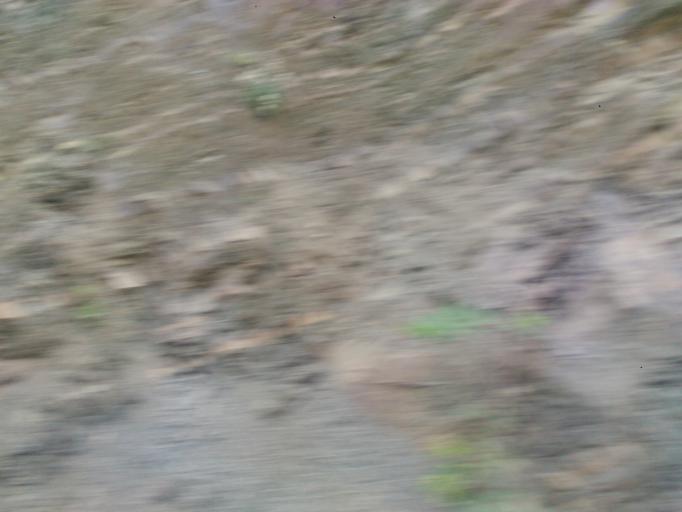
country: GE
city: Zhinvali
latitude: 42.1949
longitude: 44.8262
